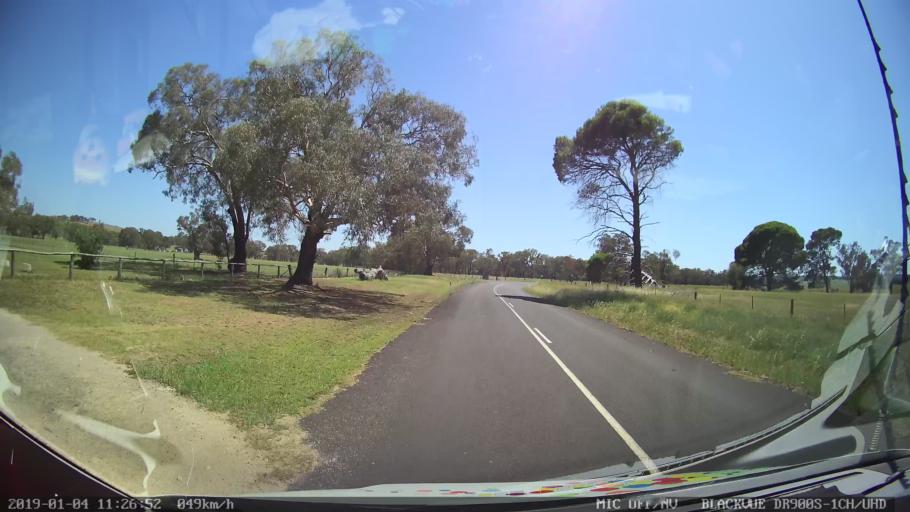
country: AU
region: New South Wales
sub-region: Cabonne
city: Molong
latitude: -33.1123
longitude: 148.7576
